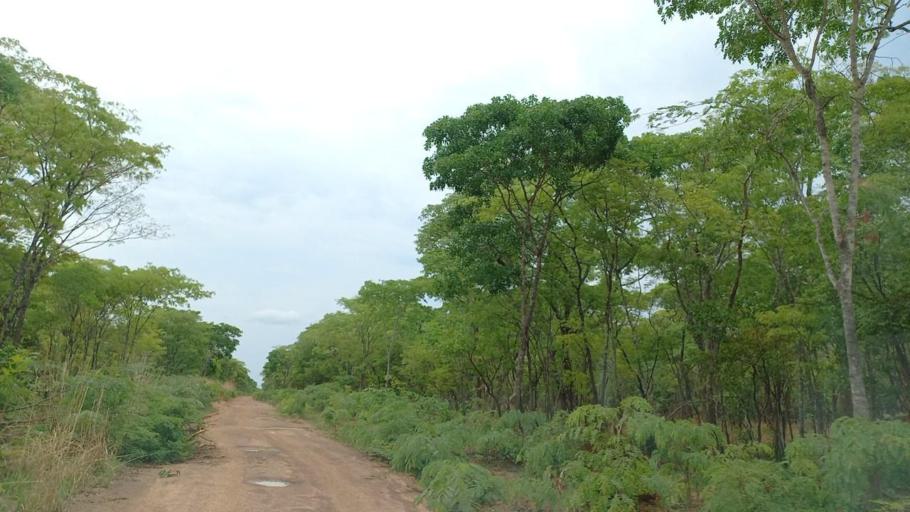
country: ZM
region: North-Western
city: Kalengwa
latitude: -13.5968
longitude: 24.9737
